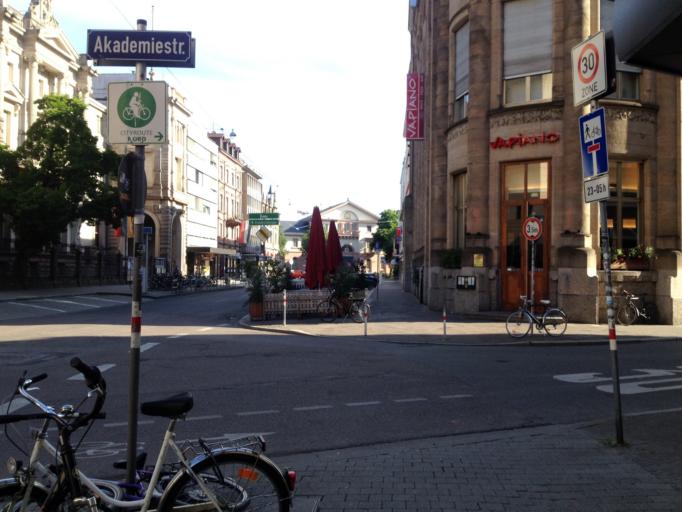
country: DE
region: Baden-Wuerttemberg
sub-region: Karlsruhe Region
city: Karlsruhe
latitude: 49.0106
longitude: 8.3952
